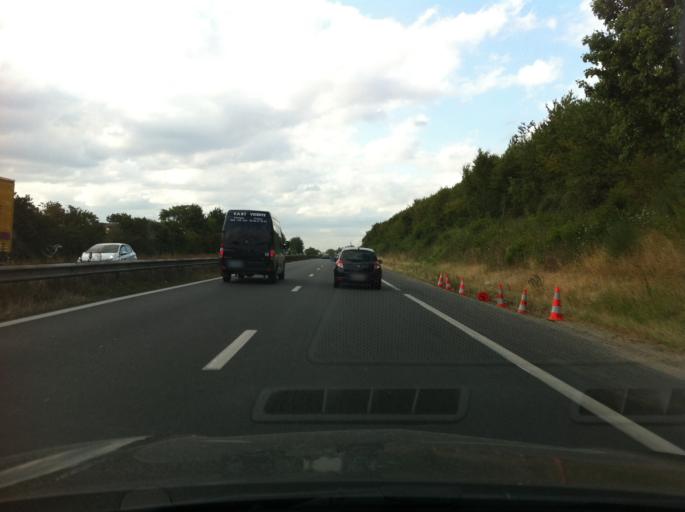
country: FR
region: Ile-de-France
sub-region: Departement de Seine-et-Marne
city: Brie-Comte-Robert
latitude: 48.6938
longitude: 2.5950
